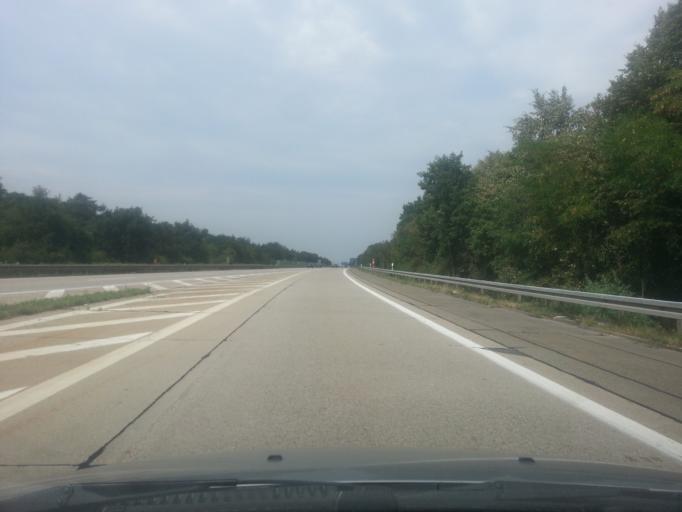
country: DE
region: Baden-Wuerttemberg
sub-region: Karlsruhe Region
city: Hockenheim
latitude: 49.3392
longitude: 8.5575
